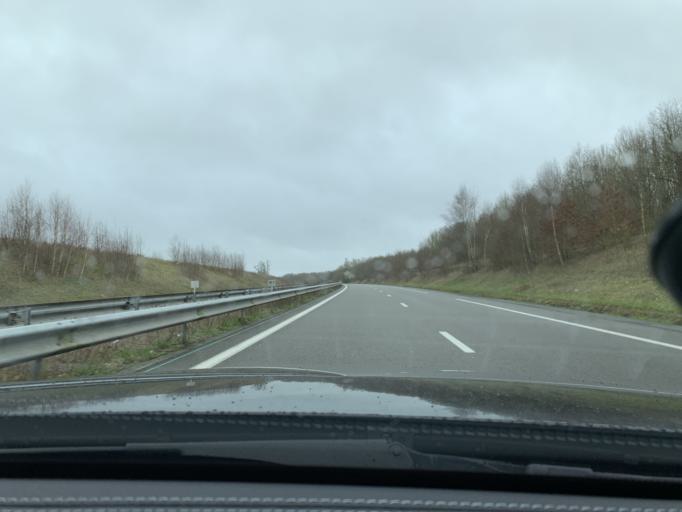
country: FR
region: Picardie
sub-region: Departement de l'Oise
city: Breteuil
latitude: 49.6657
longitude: 2.2084
